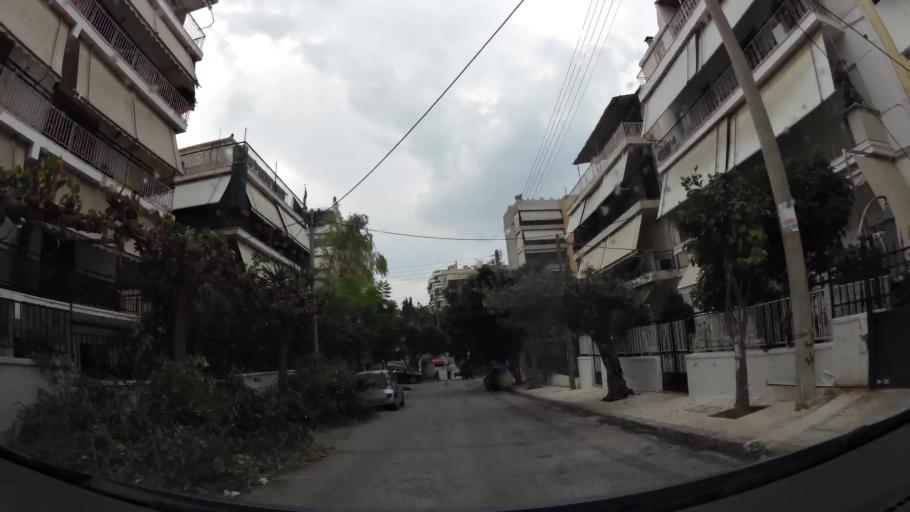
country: GR
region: Attica
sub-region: Nomarchia Athinas
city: Alimos
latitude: 37.9238
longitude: 23.7215
